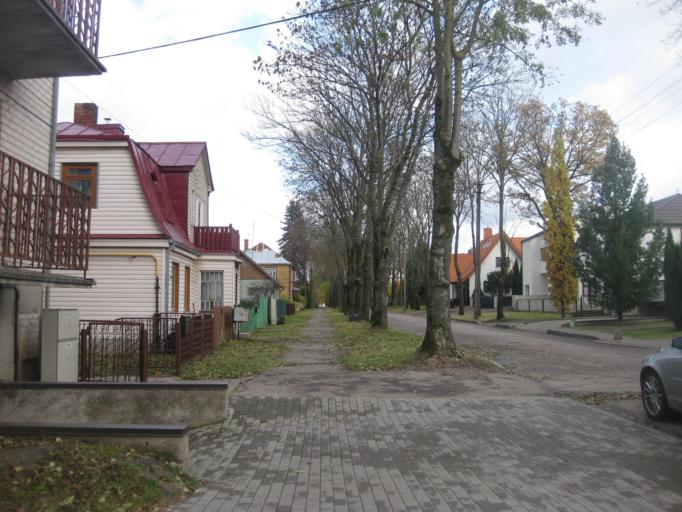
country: LT
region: Kauno apskritis
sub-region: Kaunas
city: Eiguliai
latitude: 54.9050
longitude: 23.9418
